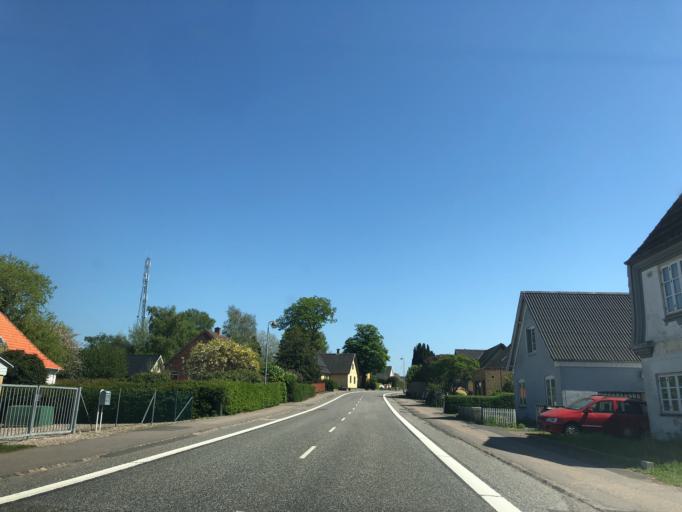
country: DK
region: Zealand
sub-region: Slagelse Kommune
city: Skaelskor
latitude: 55.3045
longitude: 11.2649
